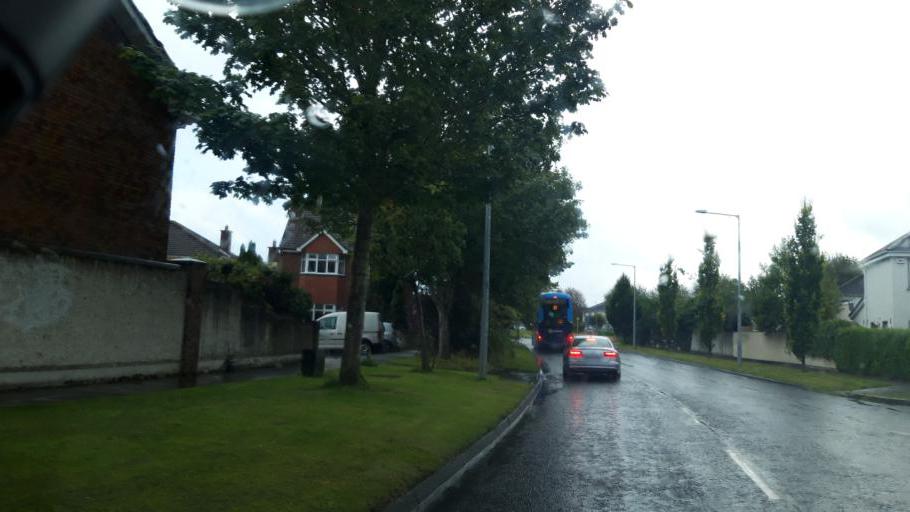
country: IE
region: Leinster
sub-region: Fingal County
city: Blanchardstown
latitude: 53.3769
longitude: -6.3823
